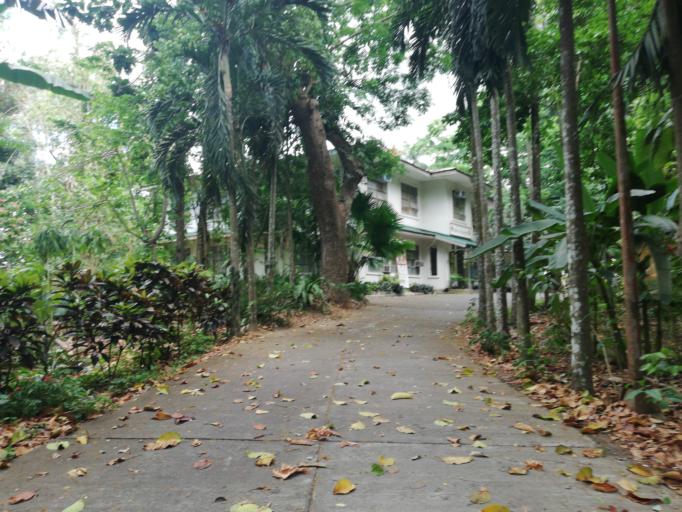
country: PH
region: Calabarzon
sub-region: Province of Laguna
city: Los Banos
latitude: 14.1564
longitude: 121.2359
